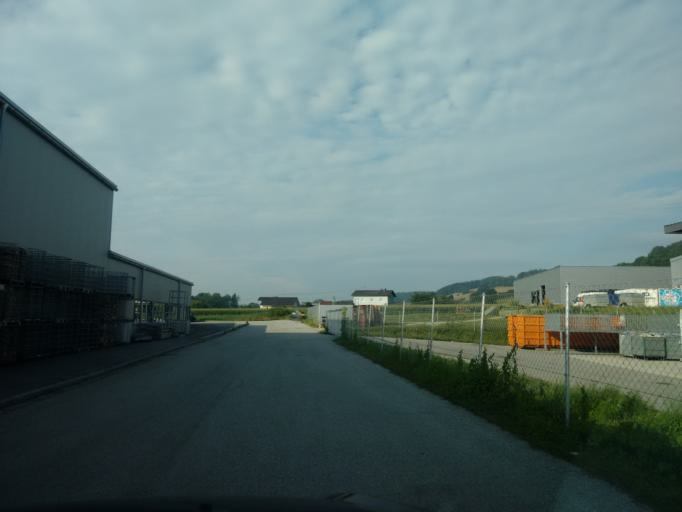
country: AT
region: Upper Austria
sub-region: Politischer Bezirk Grieskirchen
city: Bad Schallerbach
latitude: 48.2167
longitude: 13.9296
